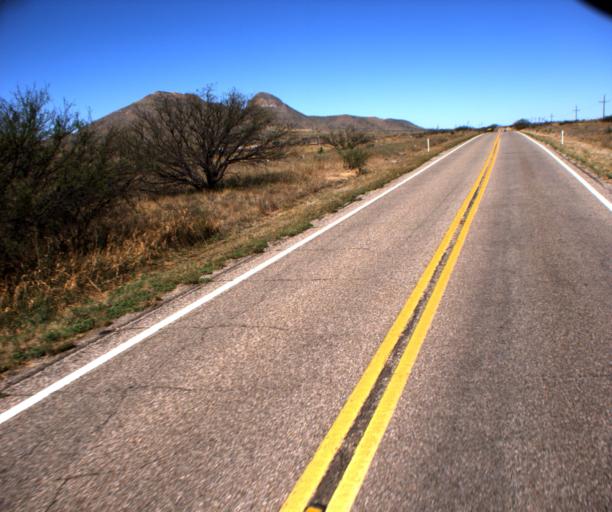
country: US
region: Arizona
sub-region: Cochise County
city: Huachuca City
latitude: 31.7095
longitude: -110.4473
